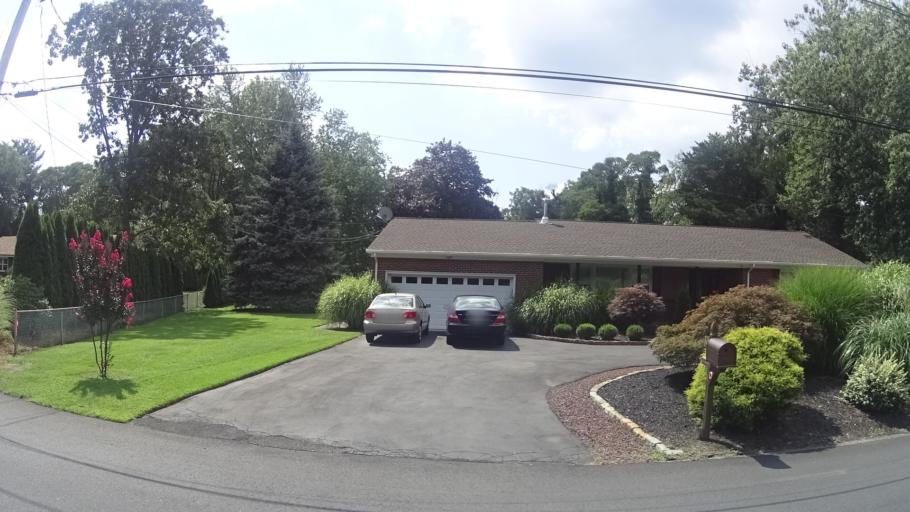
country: US
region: New Jersey
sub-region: Ocean County
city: Point Pleasant
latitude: 40.1029
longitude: -74.0840
